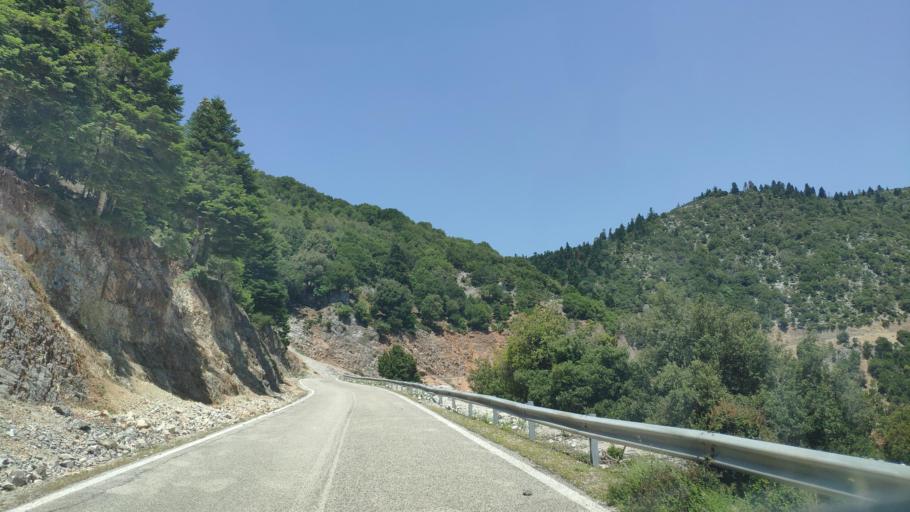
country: GR
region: West Greece
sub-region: Nomos Aitolias kai Akarnanias
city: Krikellos
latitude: 39.0292
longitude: 21.3692
